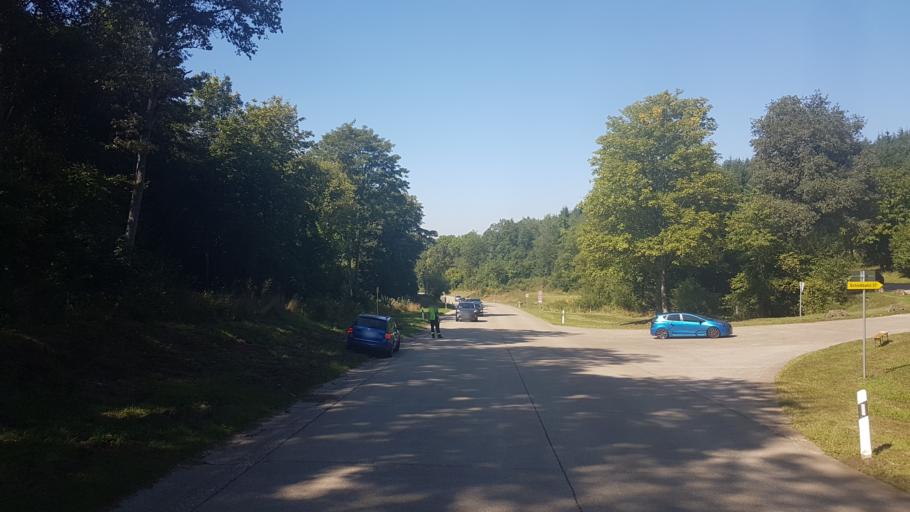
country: DE
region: Rheinland-Pfalz
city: Reichenbach
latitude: 49.6382
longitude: 7.3083
